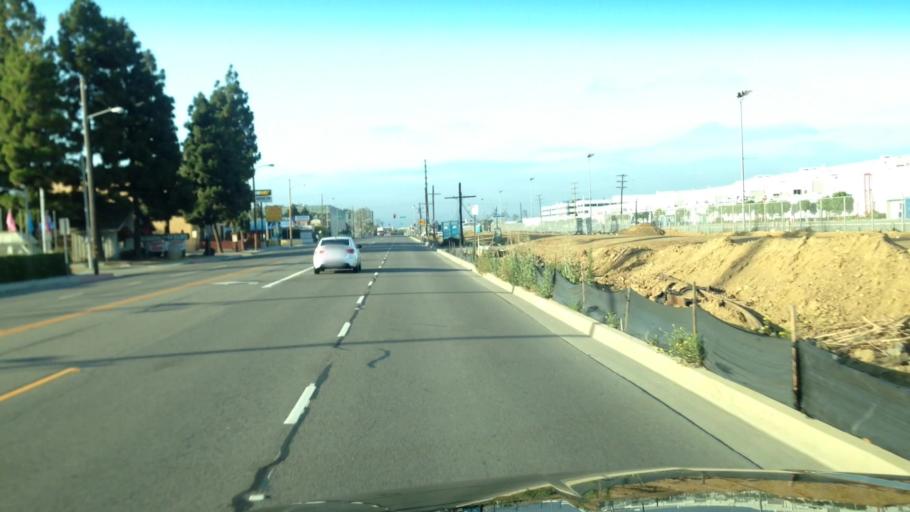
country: US
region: California
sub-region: Los Angeles County
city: Del Aire
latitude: 33.9261
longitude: -118.3786
